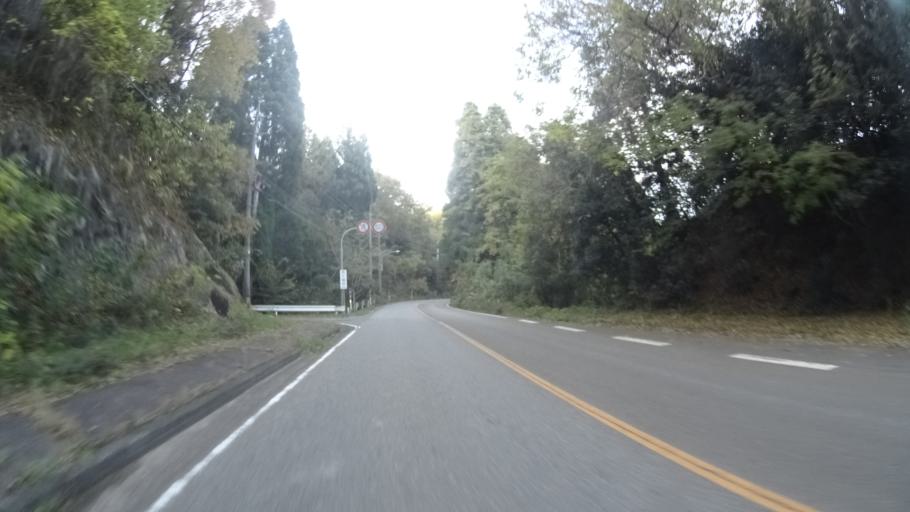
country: JP
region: Ishikawa
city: Nanao
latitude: 37.1795
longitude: 136.7131
